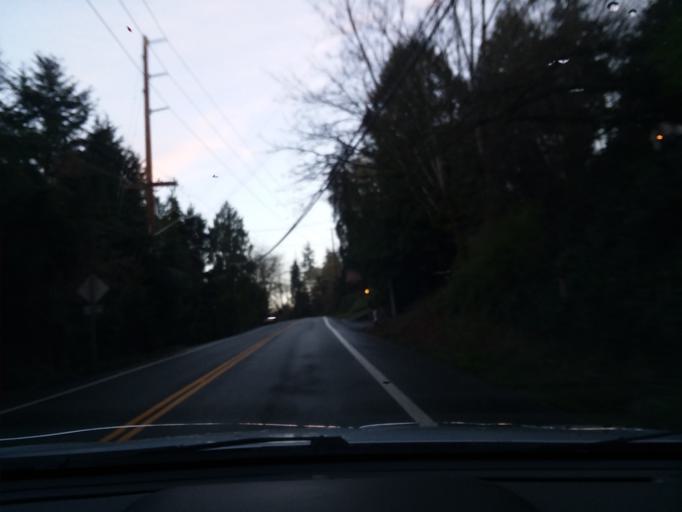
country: US
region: Washington
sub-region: King County
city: Kenmore
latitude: 47.7693
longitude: -122.2486
